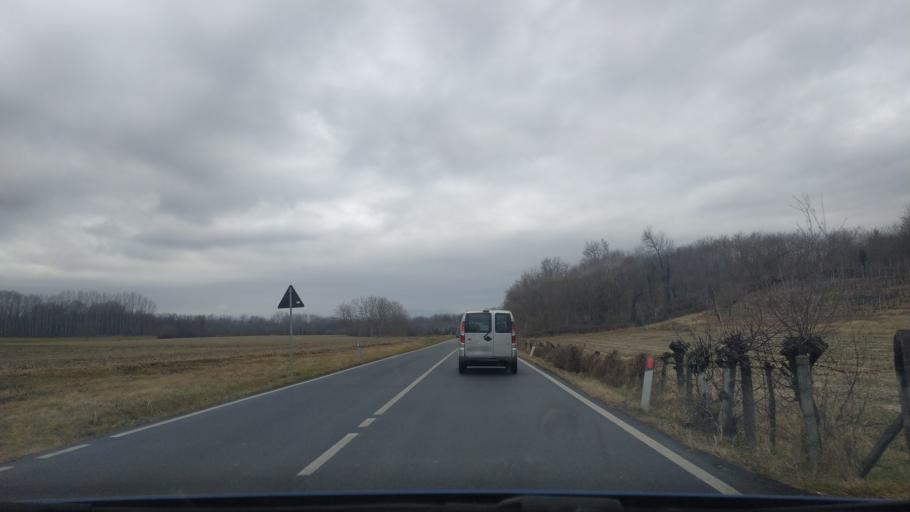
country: IT
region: Piedmont
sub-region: Provincia di Torino
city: Mercenasco
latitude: 45.3466
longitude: 7.8845
